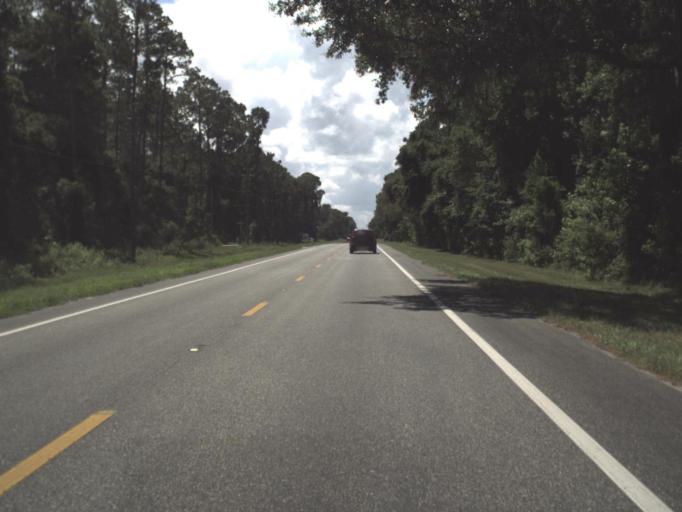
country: US
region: Florida
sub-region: Putnam County
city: Crescent City
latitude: 29.4648
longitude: -81.5256
